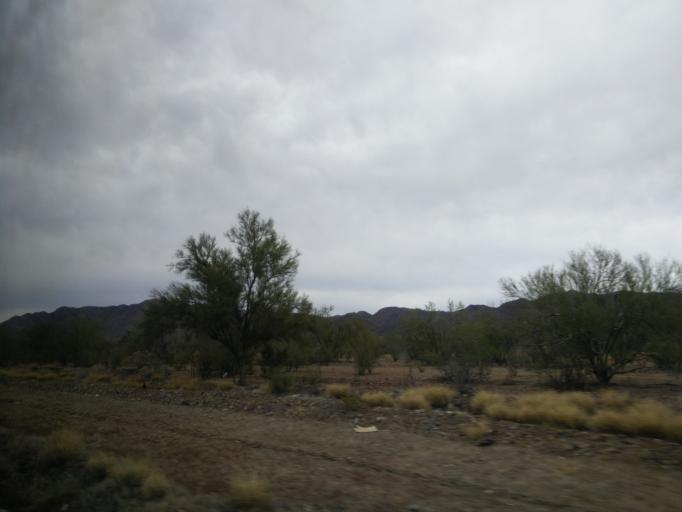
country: MX
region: Sonora
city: Hermosillo
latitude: 28.9460
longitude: -110.9620
